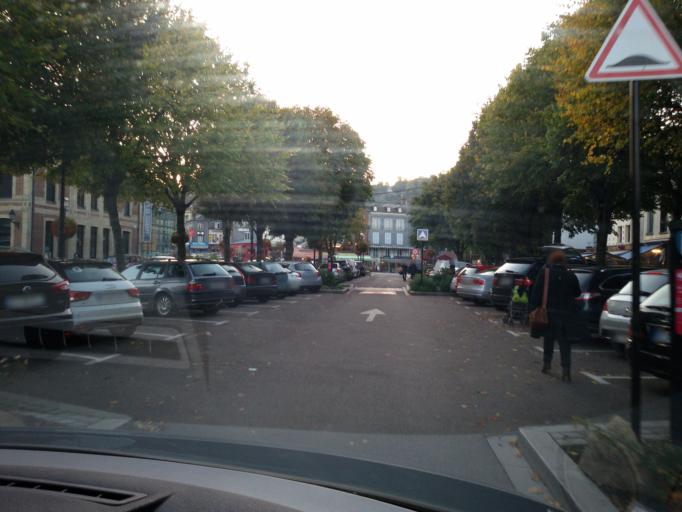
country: FR
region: Lower Normandy
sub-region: Departement du Calvados
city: Honfleur
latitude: 49.4187
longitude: 0.2353
